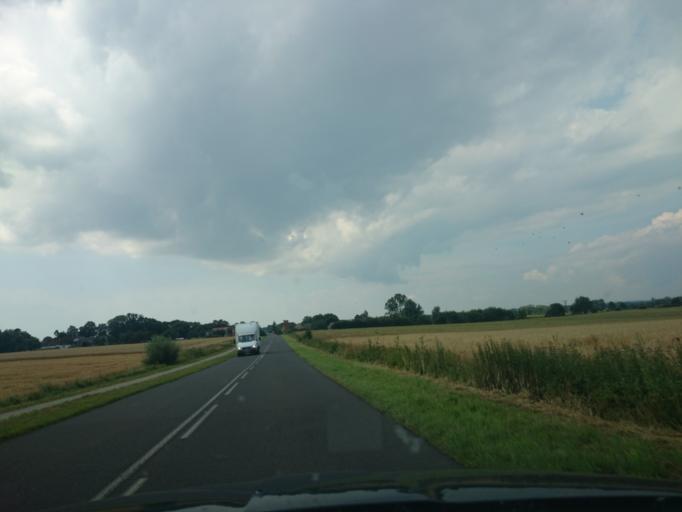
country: PL
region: West Pomeranian Voivodeship
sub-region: Powiat kamienski
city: Wolin
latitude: 53.9218
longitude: 14.6642
